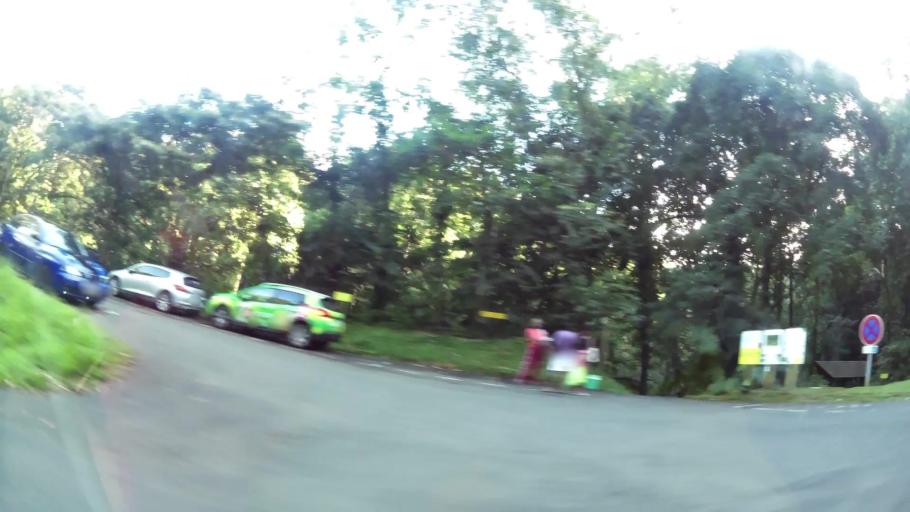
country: GP
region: Guadeloupe
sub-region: Guadeloupe
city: Bouillante
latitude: 16.1752
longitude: -61.6944
